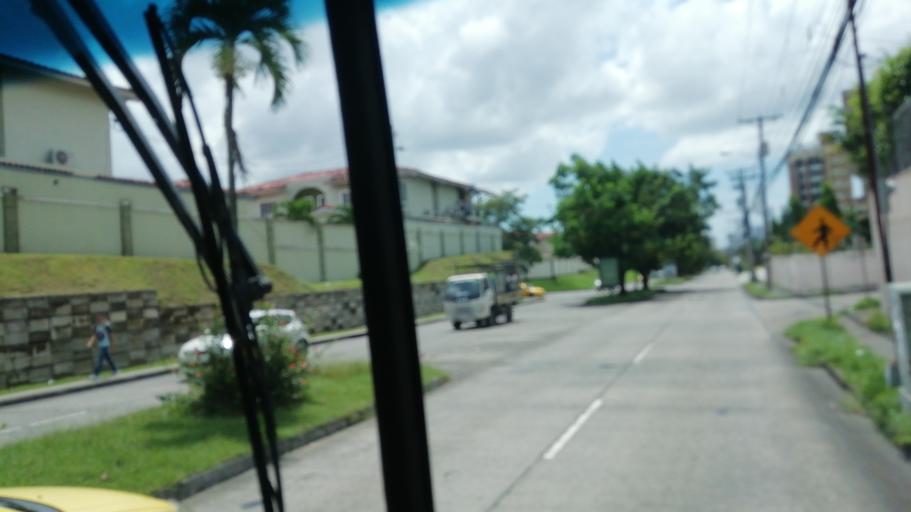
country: PA
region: Panama
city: San Miguelito
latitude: 9.0397
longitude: -79.4842
